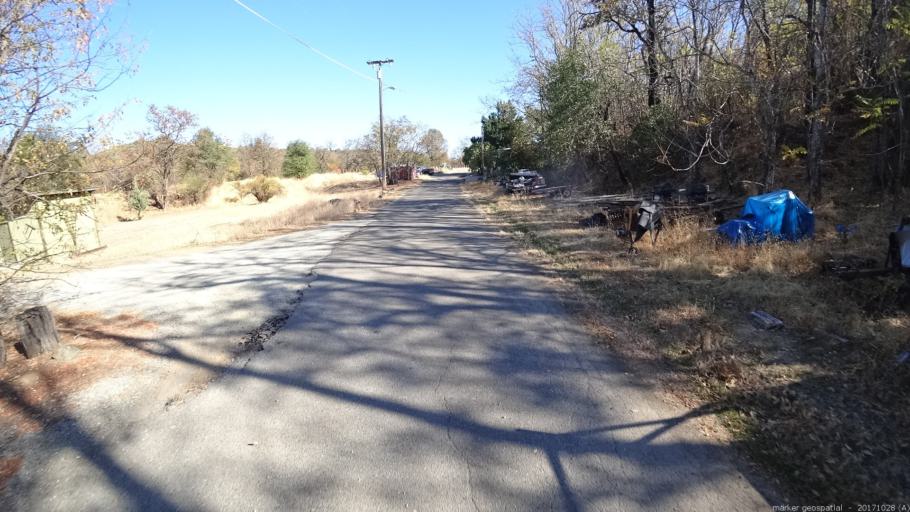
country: US
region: California
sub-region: Shasta County
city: Redding
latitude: 40.5952
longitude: -122.4411
